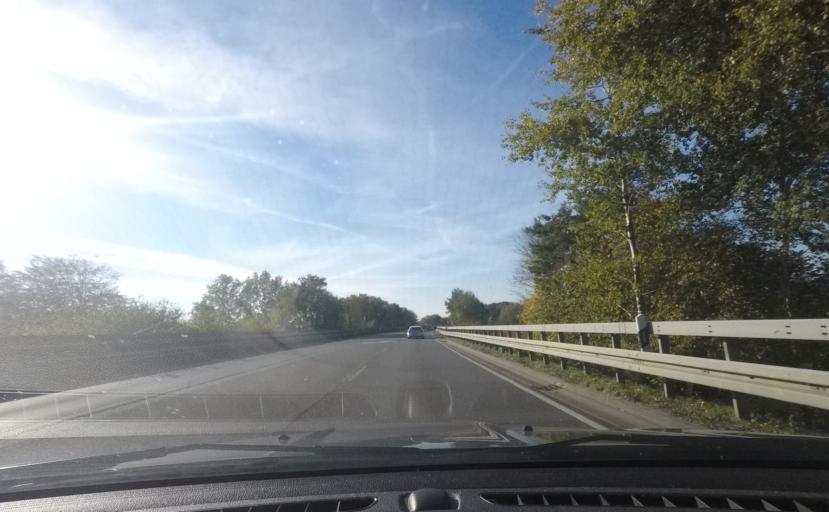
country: DE
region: North Rhine-Westphalia
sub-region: Regierungsbezirk Munster
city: Borken
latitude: 51.8300
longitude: 6.8603
